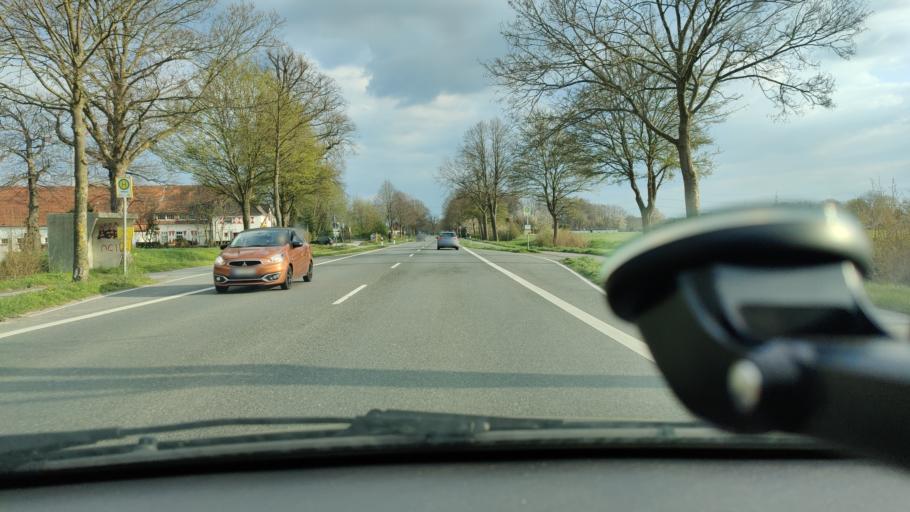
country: DE
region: North Rhine-Westphalia
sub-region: Regierungsbezirk Dusseldorf
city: Hamminkeln
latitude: 51.7092
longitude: 6.5996
